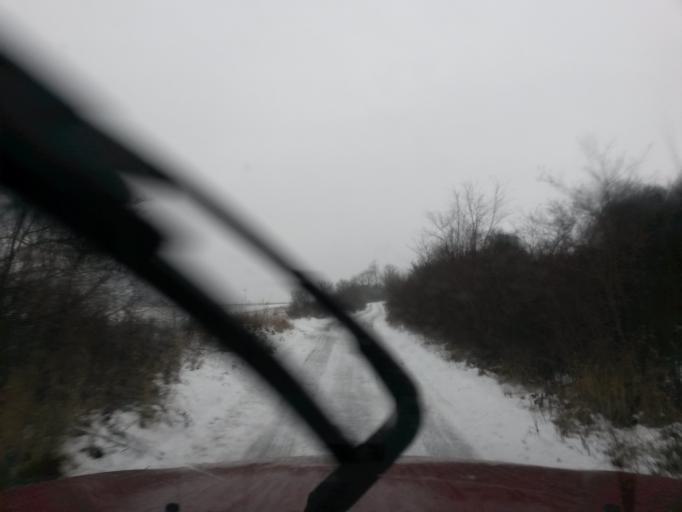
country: SK
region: Presovsky
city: Stropkov
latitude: 49.2528
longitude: 21.7523
